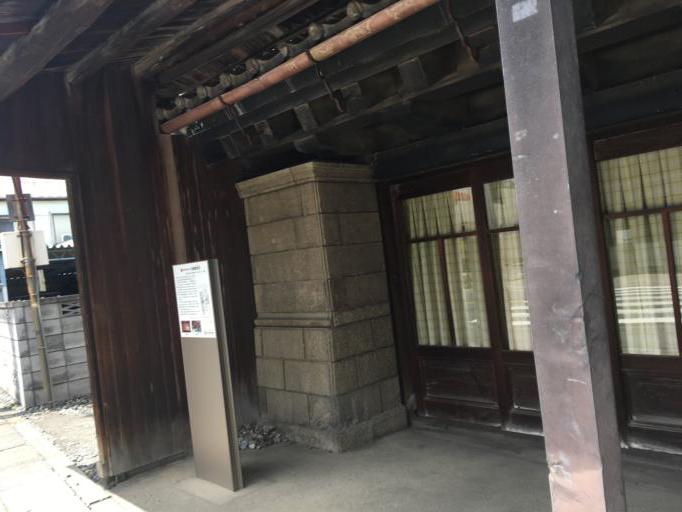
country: JP
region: Saitama
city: Okegawa
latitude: 36.0014
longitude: 139.5652
